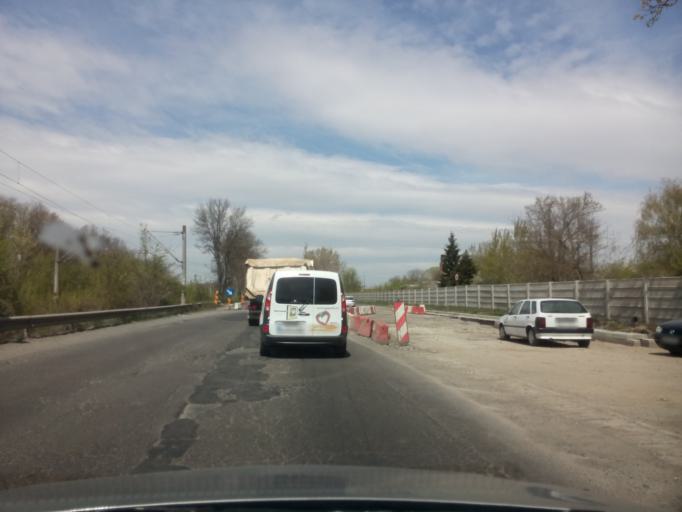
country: RO
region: Ilfov
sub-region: Comuna Pantelimon
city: Pantelimon
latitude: 44.4771
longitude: 26.2273
